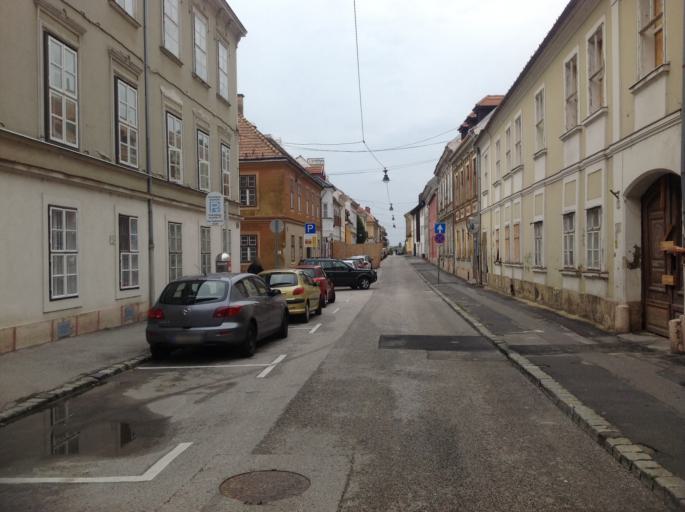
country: HU
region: Gyor-Moson-Sopron
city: Gyor
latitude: 47.6892
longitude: 17.6361
